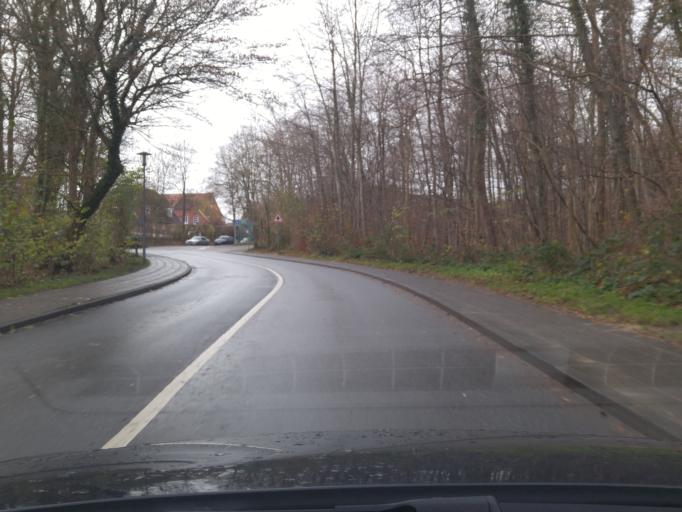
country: DE
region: Schleswig-Holstein
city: Timmendorfer Strand
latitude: 53.9998
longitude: 10.7724
